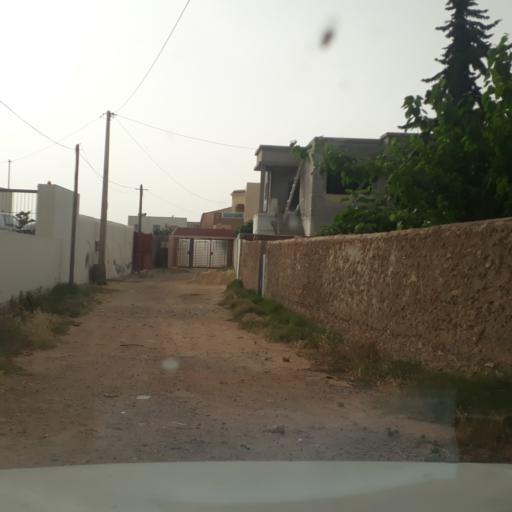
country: TN
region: Safaqis
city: Al Qarmadah
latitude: 34.8160
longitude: 10.7728
